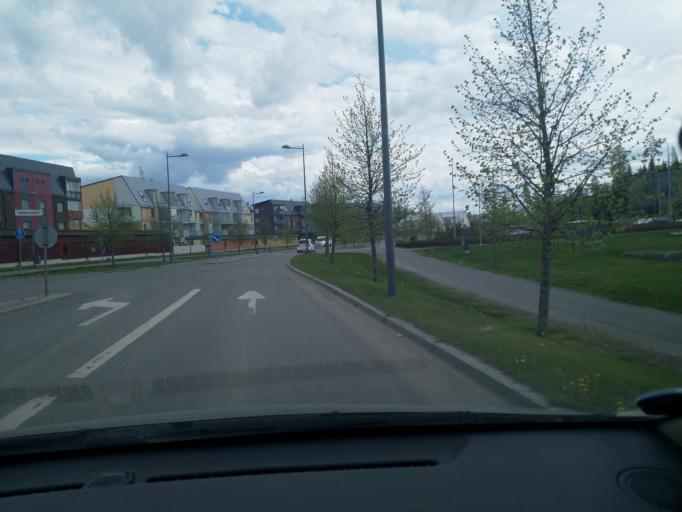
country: FI
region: Pirkanmaa
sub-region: Tampere
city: Tampere
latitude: 61.4385
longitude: 23.8115
